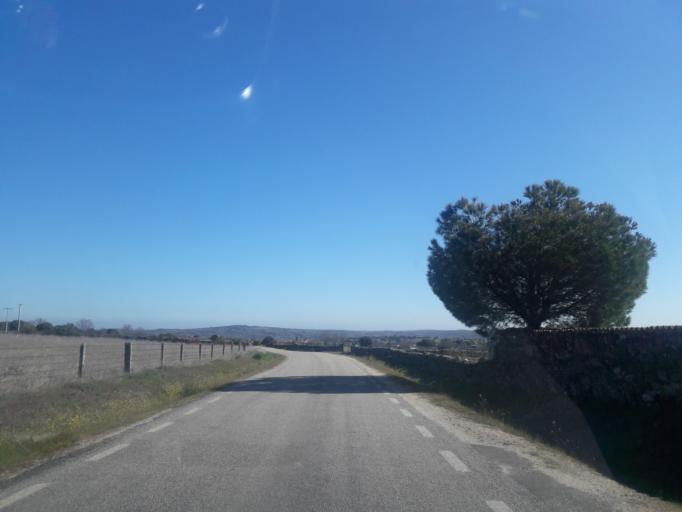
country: ES
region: Castille and Leon
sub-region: Provincia de Salamanca
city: Cabeza del Caballo
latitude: 41.1662
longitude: -6.5239
